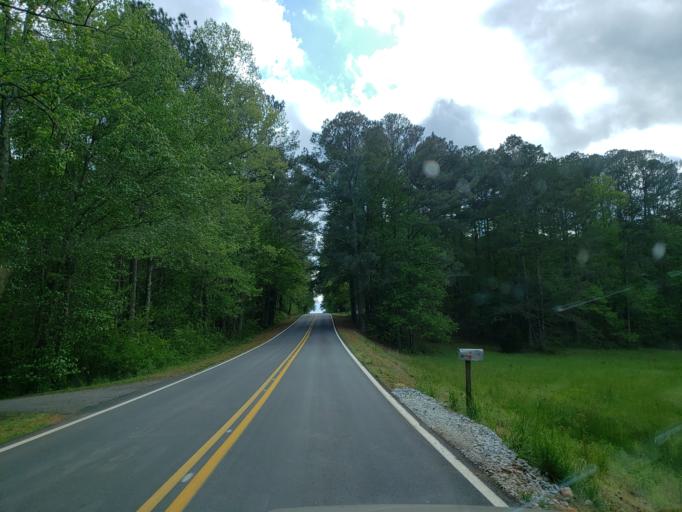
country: US
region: Georgia
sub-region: Carroll County
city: Mount Zion
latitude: 33.6785
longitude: -85.2209
